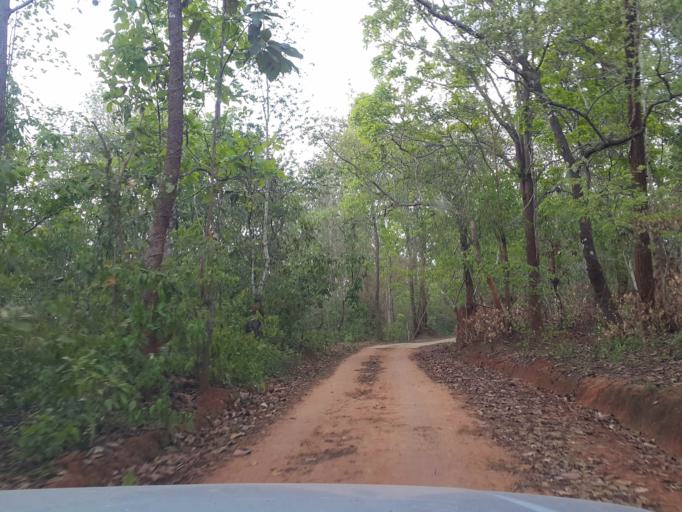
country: TH
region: Chiang Mai
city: Wiang Haeng
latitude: 19.3687
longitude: 98.7183
